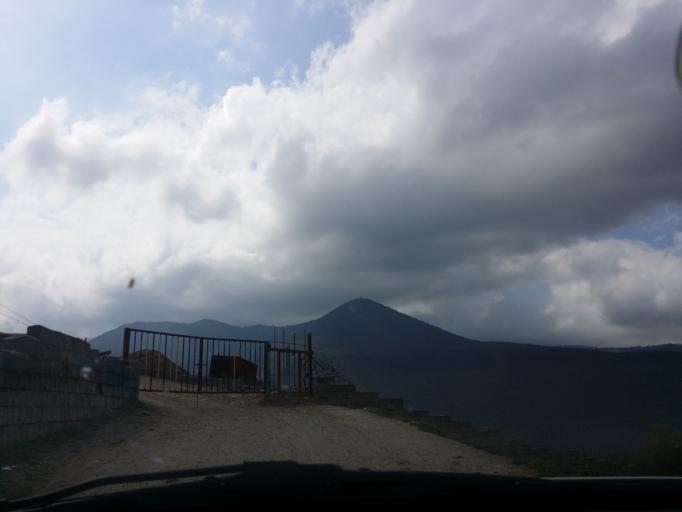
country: IR
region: Mazandaran
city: `Abbasabad
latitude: 36.4853
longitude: 51.1472
